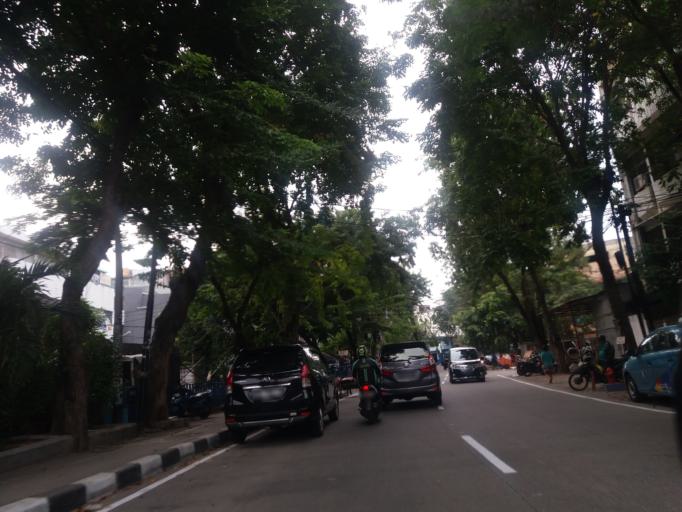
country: ID
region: Jakarta Raya
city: Jakarta
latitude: -6.1466
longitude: 106.8318
